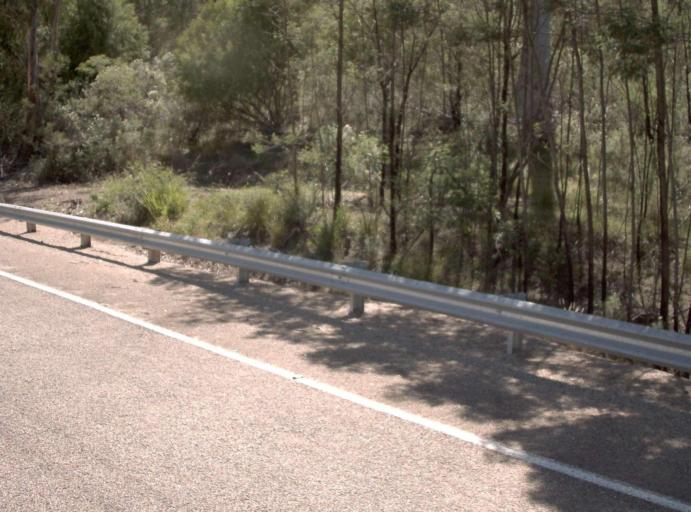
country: AU
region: Victoria
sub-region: East Gippsland
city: Lakes Entrance
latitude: -37.3911
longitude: 148.2190
